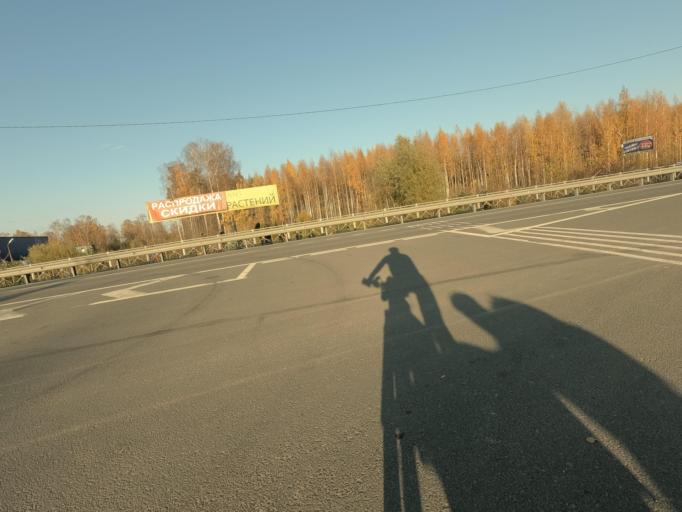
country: RU
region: Leningrad
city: Kirovsk
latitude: 59.8558
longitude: 31.0127
